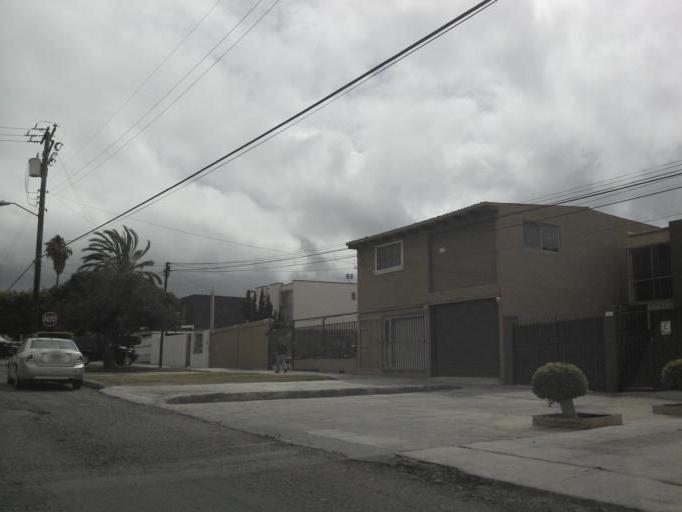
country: MX
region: Baja California
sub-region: Tijuana
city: La Esperanza [Granjas Familiares]
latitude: 32.5176
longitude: -117.1124
